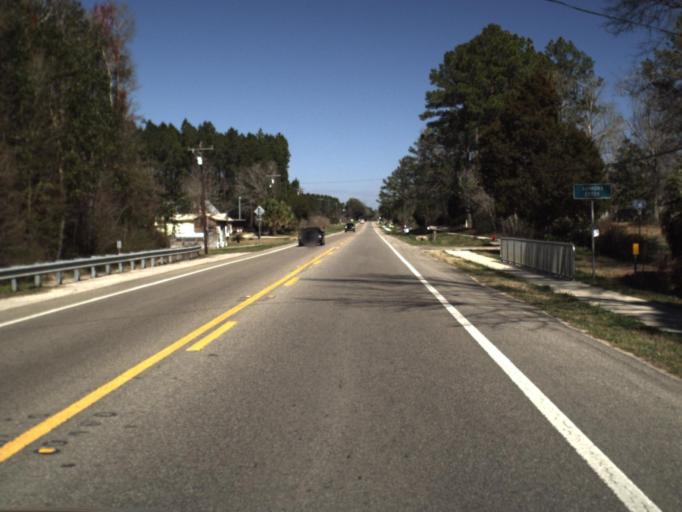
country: US
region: Florida
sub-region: Calhoun County
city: Blountstown
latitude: 30.4588
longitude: -85.0449
